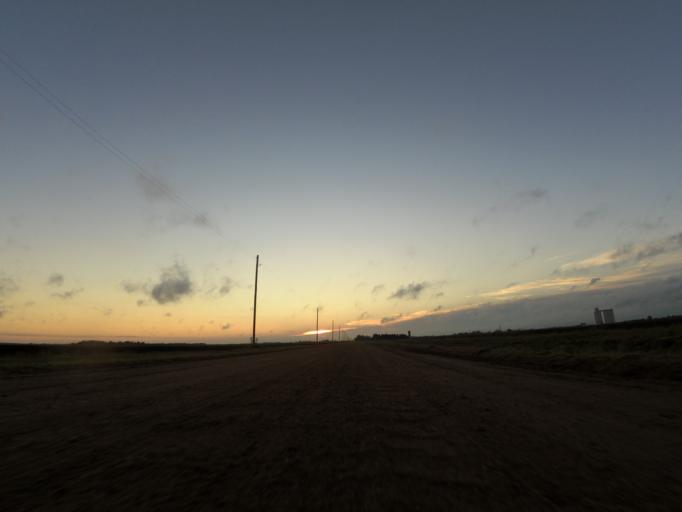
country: US
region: Kansas
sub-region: Reno County
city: South Hutchinson
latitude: 38.0135
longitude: -98.0259
